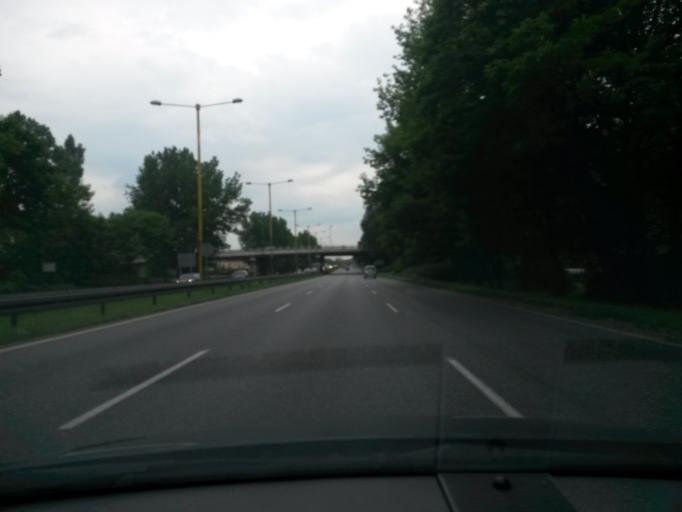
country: PL
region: Silesian Voivodeship
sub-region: Czestochowa
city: Czestochowa
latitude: 50.8139
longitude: 19.1373
